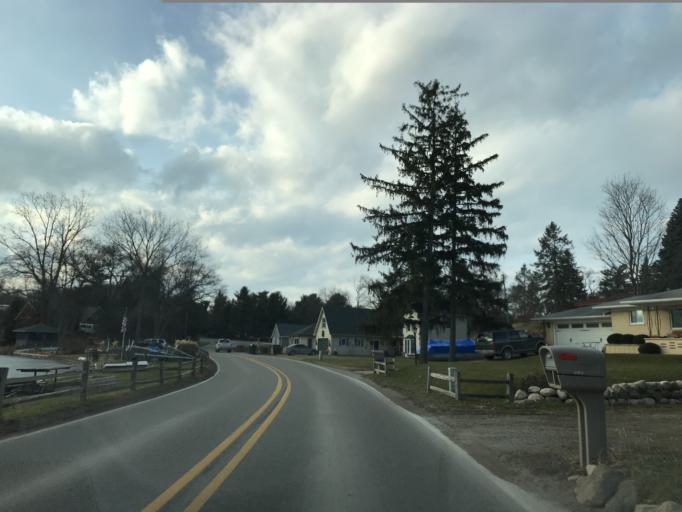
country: US
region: Michigan
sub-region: Livingston County
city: Whitmore Lake
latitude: 42.4711
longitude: -83.7238
